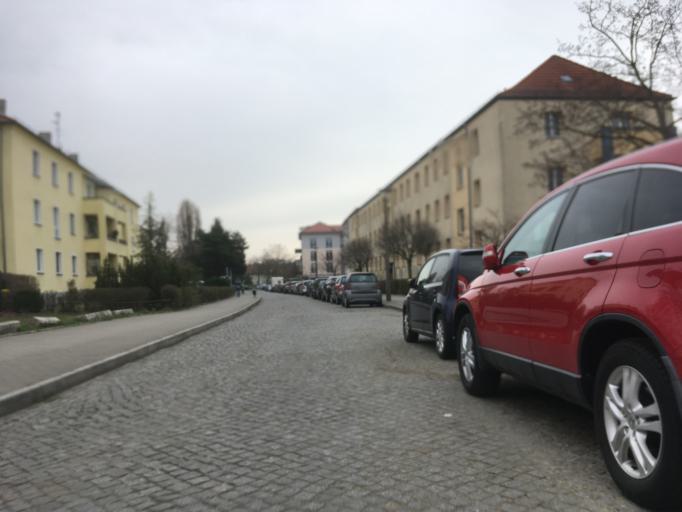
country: DE
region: Berlin
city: Johannisthal
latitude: 52.4480
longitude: 13.5041
